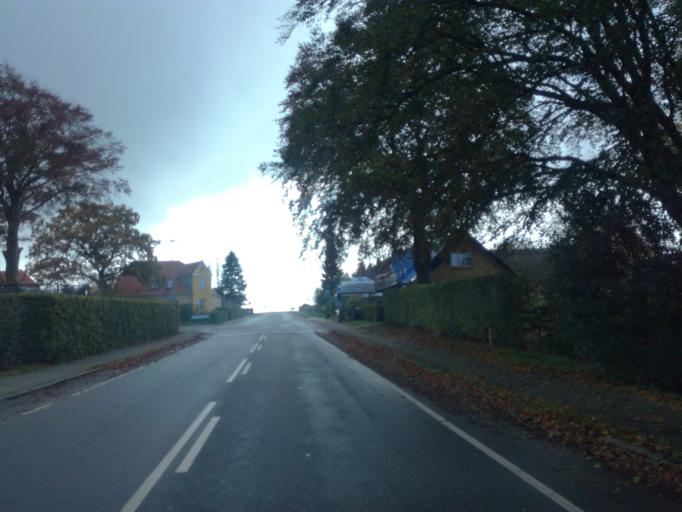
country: DK
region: South Denmark
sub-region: Vejle Kommune
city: Vejle
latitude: 55.6719
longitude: 9.5748
